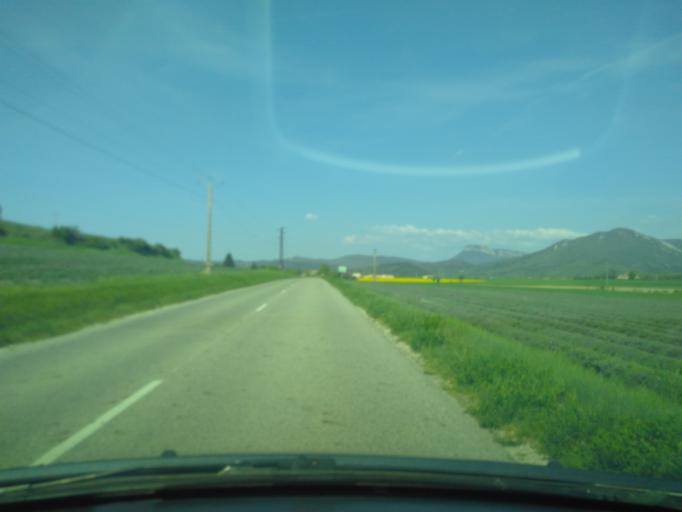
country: FR
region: Rhone-Alpes
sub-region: Departement de la Drome
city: La Begude-de-Mazenc
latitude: 44.5851
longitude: 4.9546
